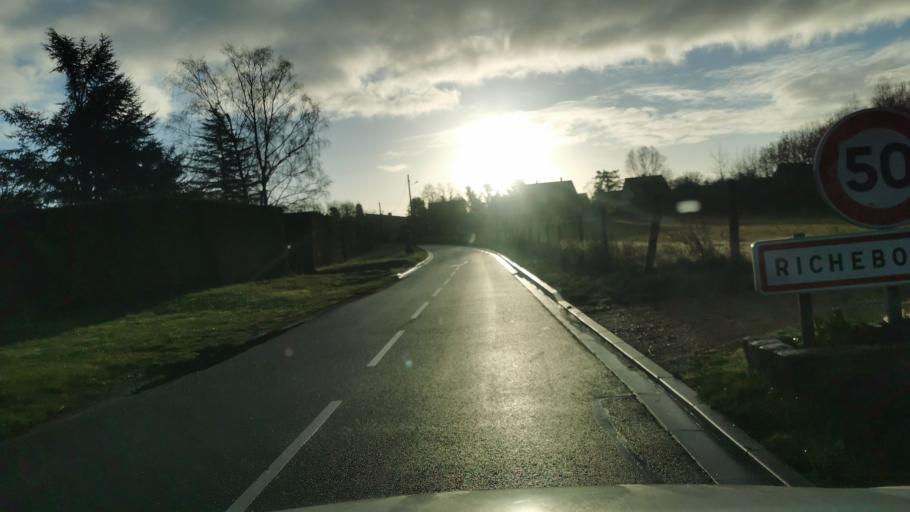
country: FR
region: Ile-de-France
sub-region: Departement des Yvelines
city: Bazainville
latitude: 48.8275
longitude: 1.6306
